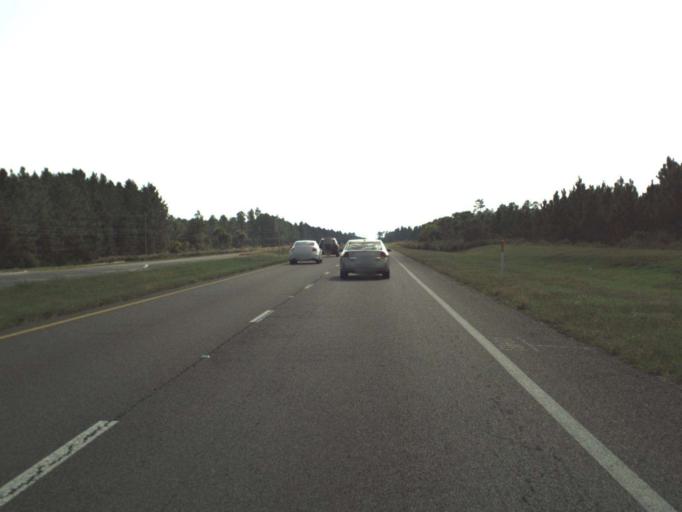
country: US
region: Florida
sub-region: Bay County
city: Laguna Beach
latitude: 30.2552
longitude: -85.8771
